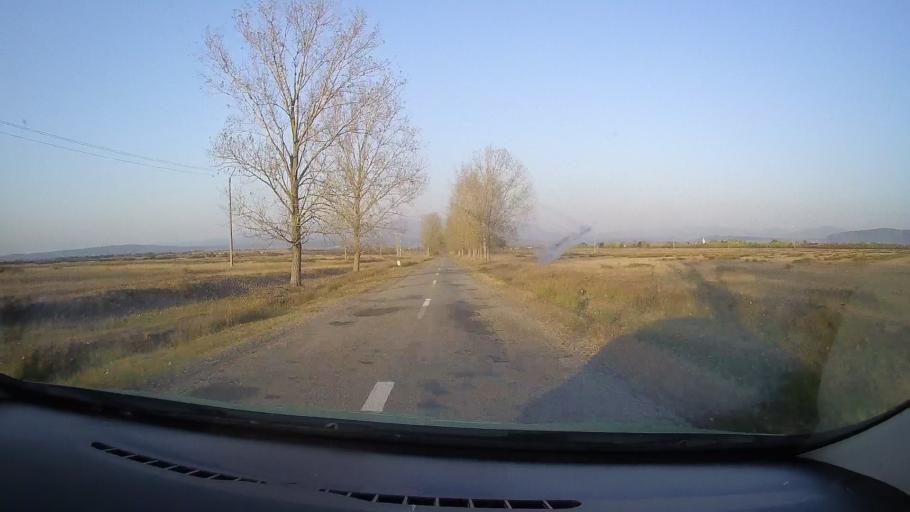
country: RO
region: Arad
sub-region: Comuna Barsa
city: Barsa
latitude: 46.3795
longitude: 22.0568
